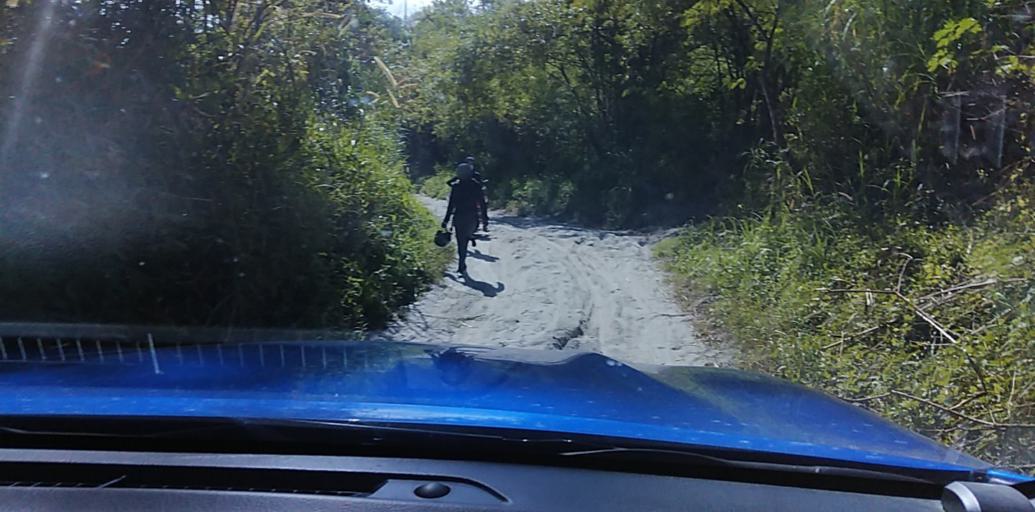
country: PH
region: Central Luzon
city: Santol
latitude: 15.1712
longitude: 120.4791
